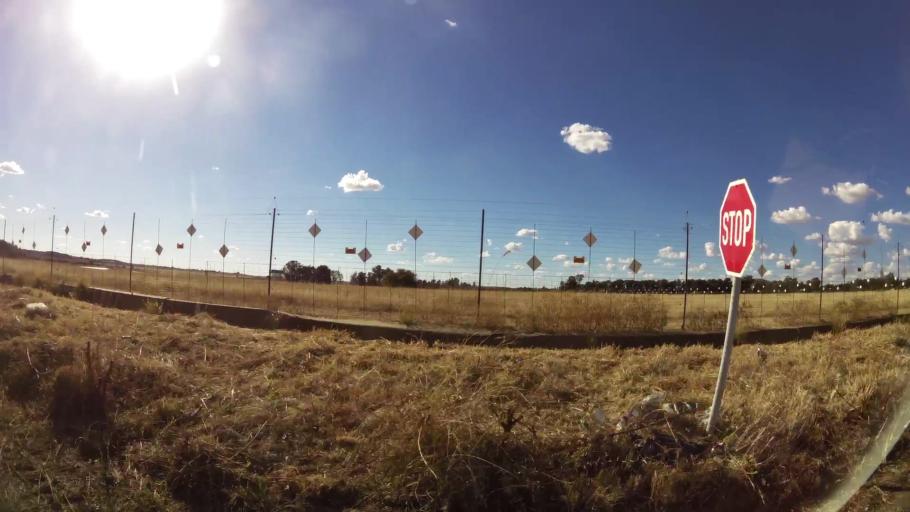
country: ZA
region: North-West
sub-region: Dr Kenneth Kaunda District Municipality
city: Klerksdorp
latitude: -26.8174
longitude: 26.6576
